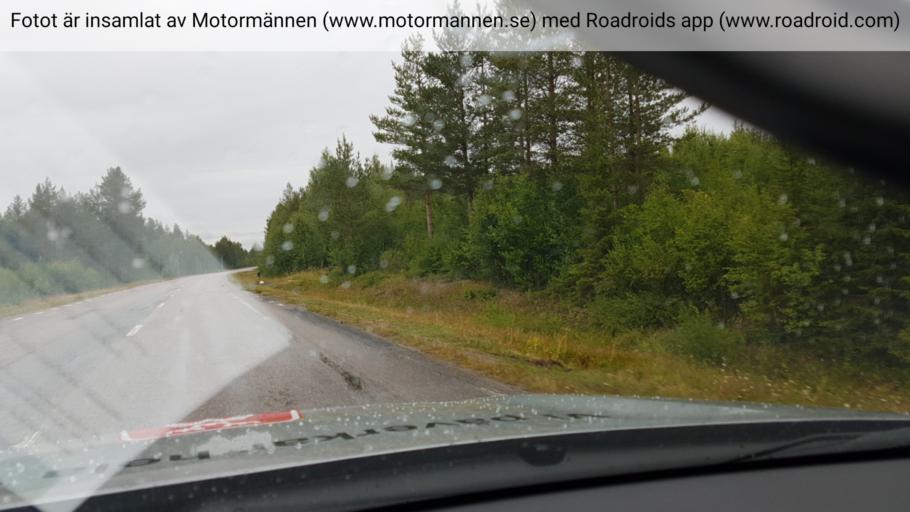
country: SE
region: Norrbotten
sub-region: Alvsbyns Kommun
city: AElvsbyn
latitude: 66.2087
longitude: 20.8765
